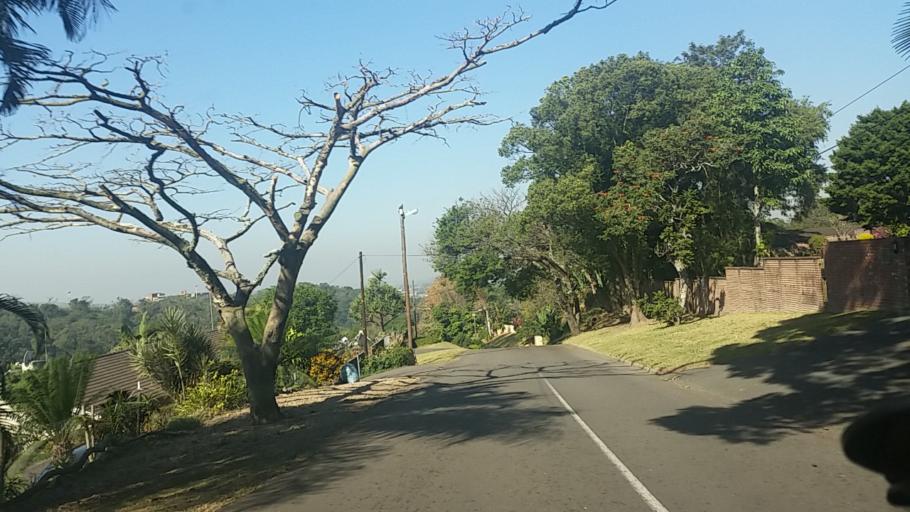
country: ZA
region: KwaZulu-Natal
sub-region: eThekwini Metropolitan Municipality
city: Berea
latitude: -29.8544
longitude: 30.9051
